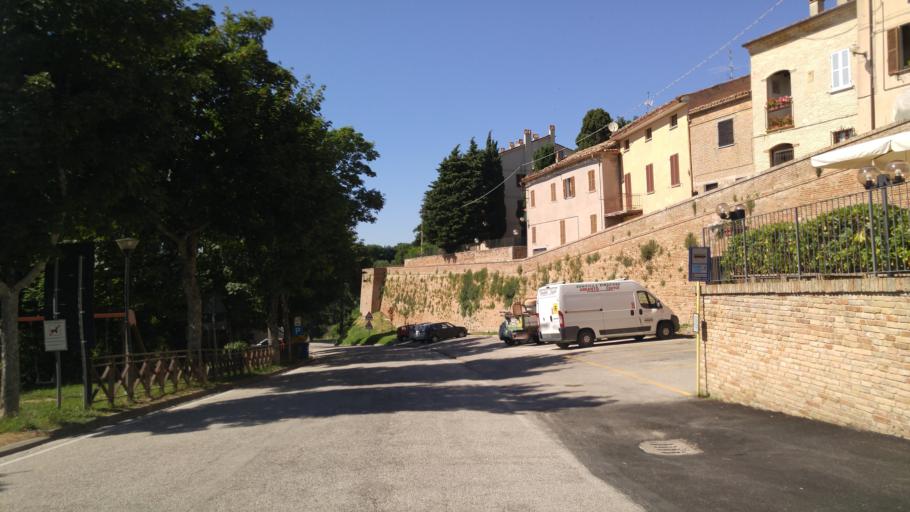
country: IT
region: The Marches
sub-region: Provincia di Pesaro e Urbino
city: Mombaroccio
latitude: 43.7957
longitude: 12.8539
